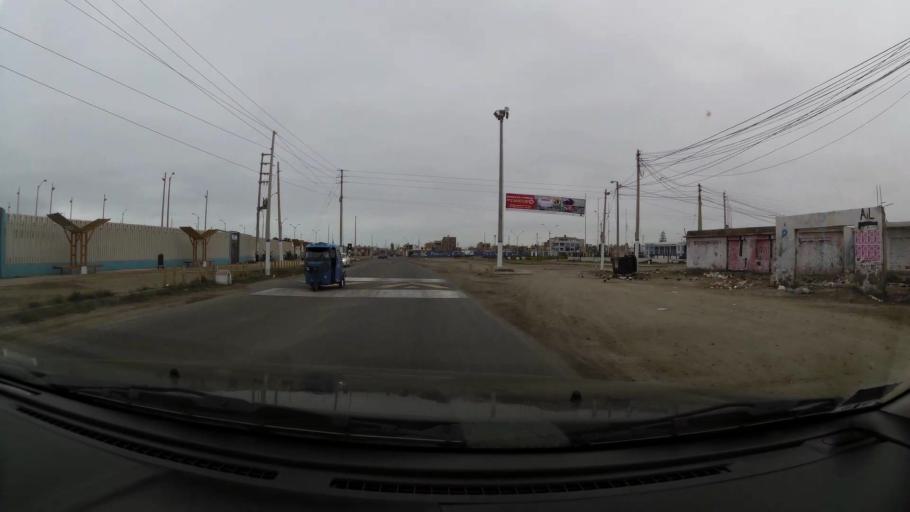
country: PE
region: Ica
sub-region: Provincia de Pisco
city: Pisco
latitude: -13.7181
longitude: -76.2199
